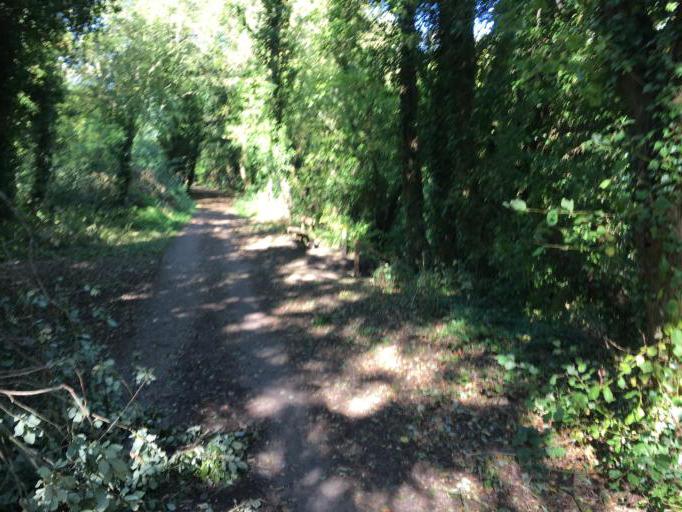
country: GB
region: England
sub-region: Warwickshire
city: Kenilworth
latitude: 52.3788
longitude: -1.6034
